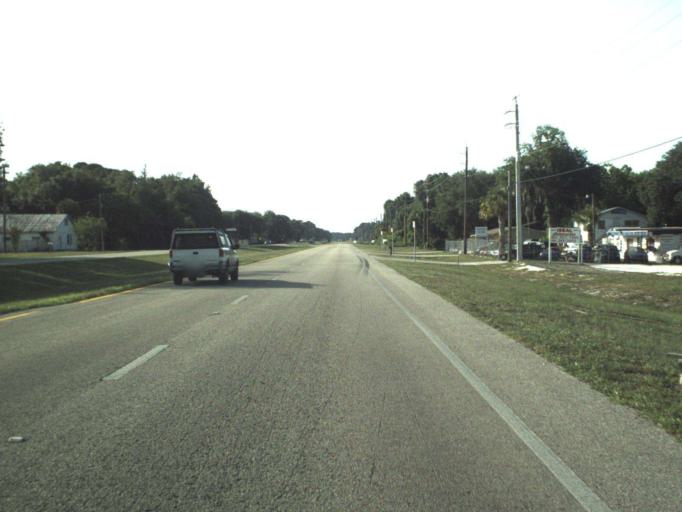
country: US
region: Florida
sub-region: Volusia County
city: Oak Hill
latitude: 28.8926
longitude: -80.8603
